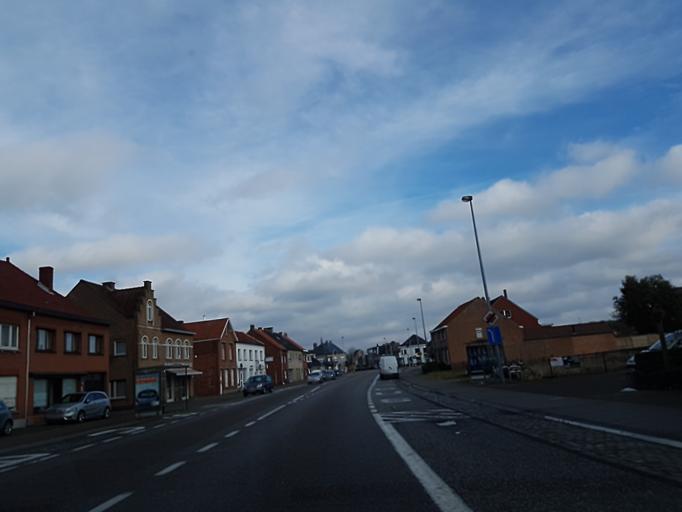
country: BE
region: Flanders
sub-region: Provincie Antwerpen
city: Westerlo
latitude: 51.0965
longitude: 4.9425
